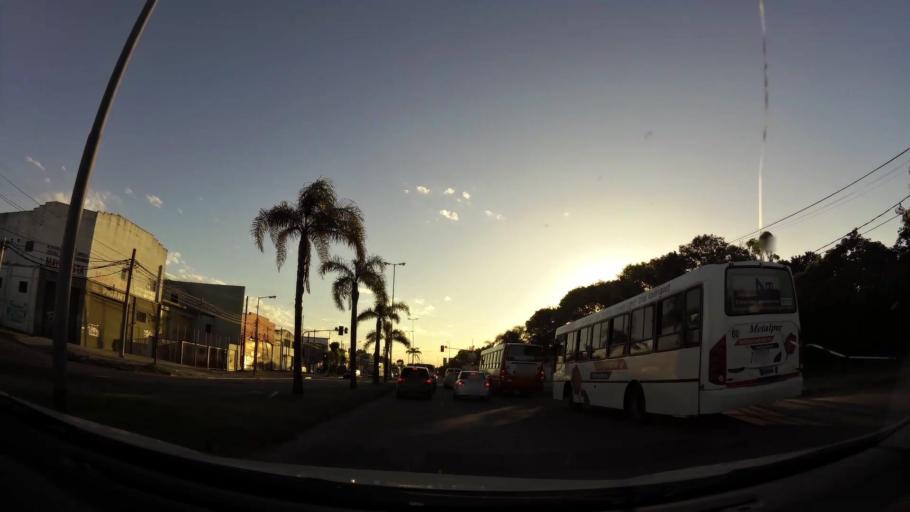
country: AR
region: Buenos Aires
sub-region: Partido de Tigre
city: Tigre
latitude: -34.4409
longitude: -58.5751
